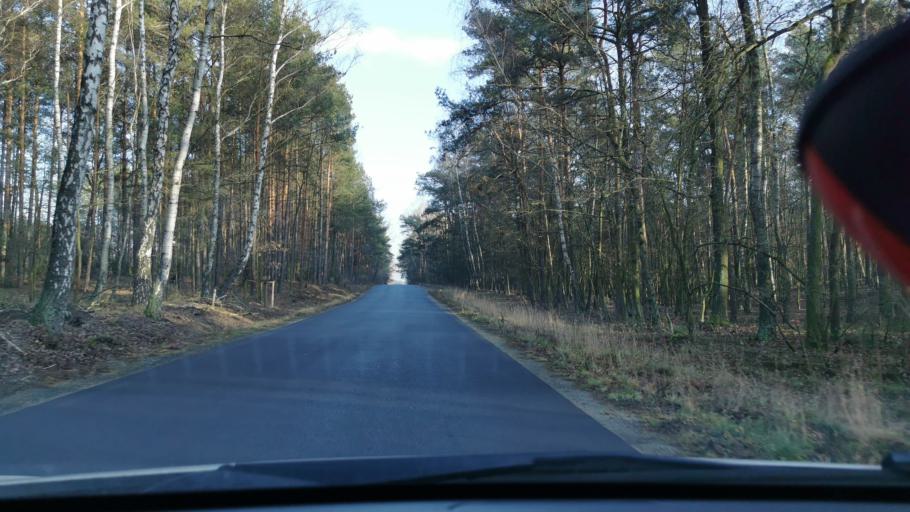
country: PL
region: Greater Poland Voivodeship
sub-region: Powiat kaliski
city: Opatowek
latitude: 51.6600
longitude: 18.2714
